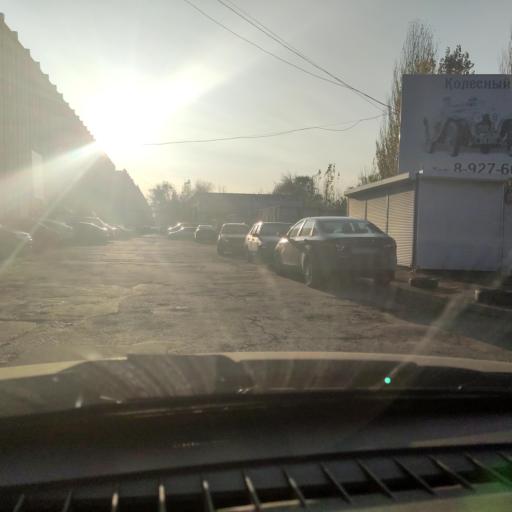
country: RU
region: Samara
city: Tol'yatti
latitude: 53.5422
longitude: 49.3130
